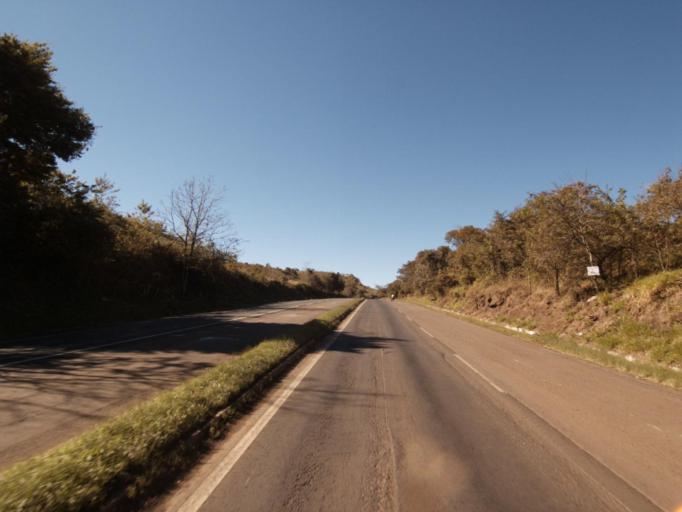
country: BR
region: Santa Catarina
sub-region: Chapeco
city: Chapeco
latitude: -26.9360
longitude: -52.7999
